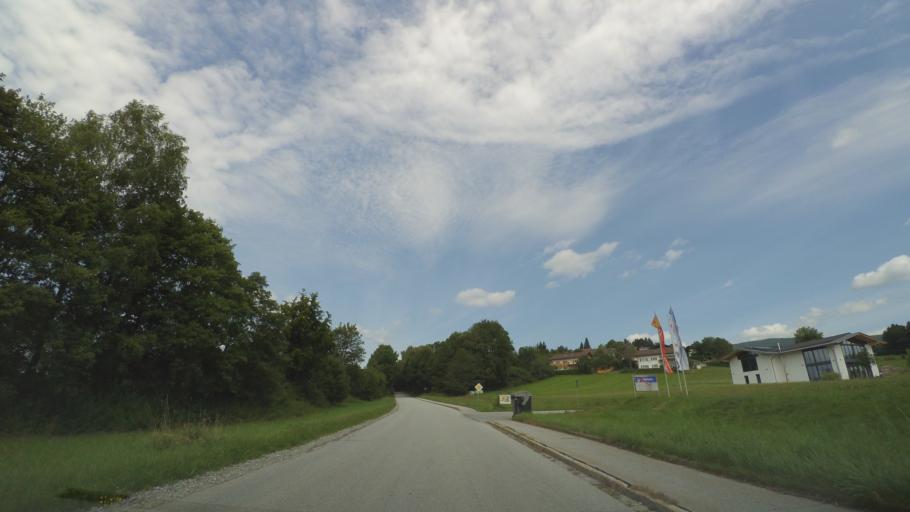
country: DE
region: Bavaria
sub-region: Lower Bavaria
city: Arnbruck
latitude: 49.1221
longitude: 12.9992
